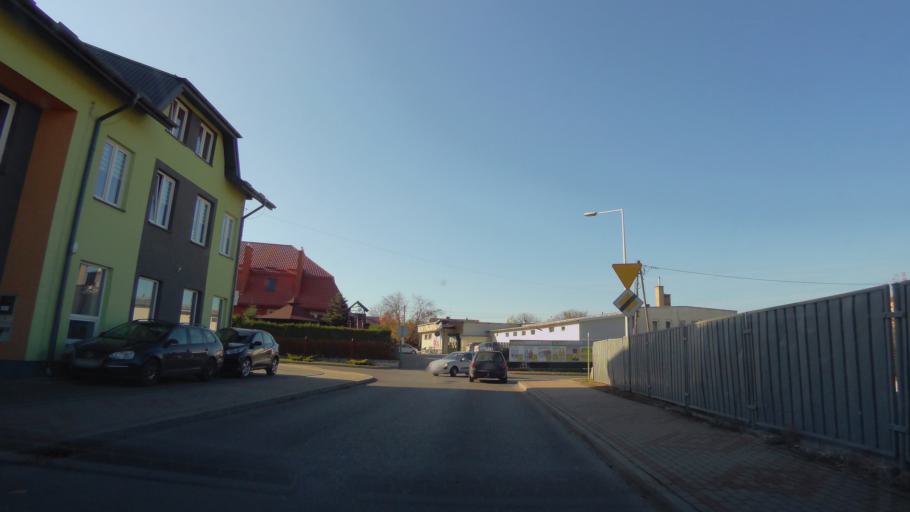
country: PL
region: Subcarpathian Voivodeship
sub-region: Powiat lezajski
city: Lezajsk
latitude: 50.2633
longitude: 22.4249
